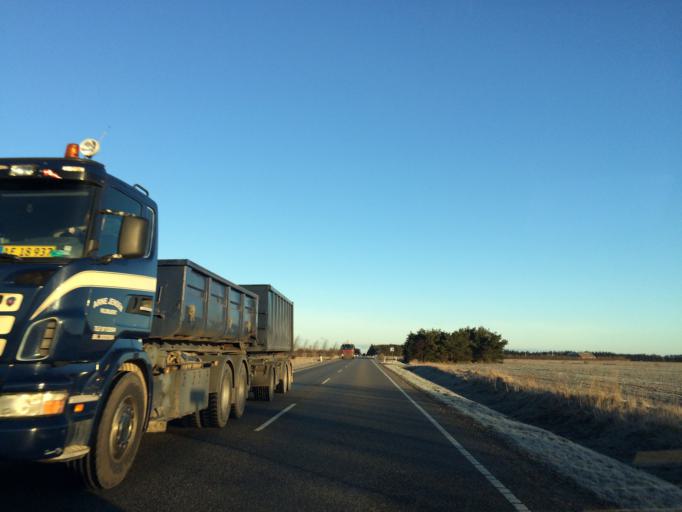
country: DK
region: Central Jutland
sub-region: Holstebro Kommune
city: Ulfborg
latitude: 56.3889
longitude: 8.3232
